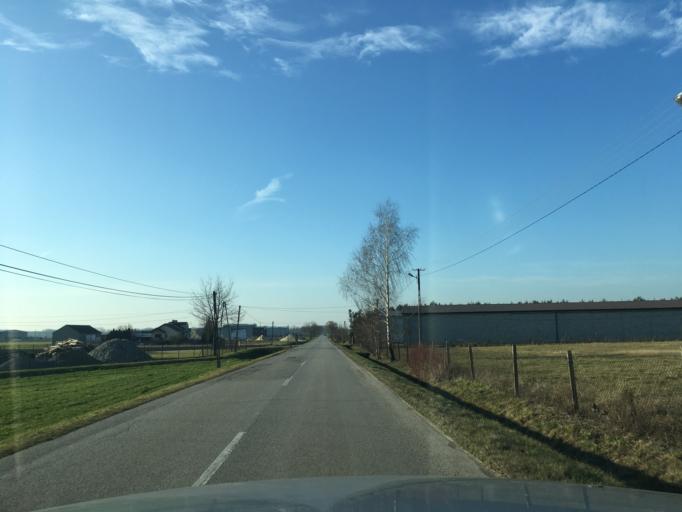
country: PL
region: Masovian Voivodeship
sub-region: Powiat pruszkowski
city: Nadarzyn
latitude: 52.0406
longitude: 20.8131
